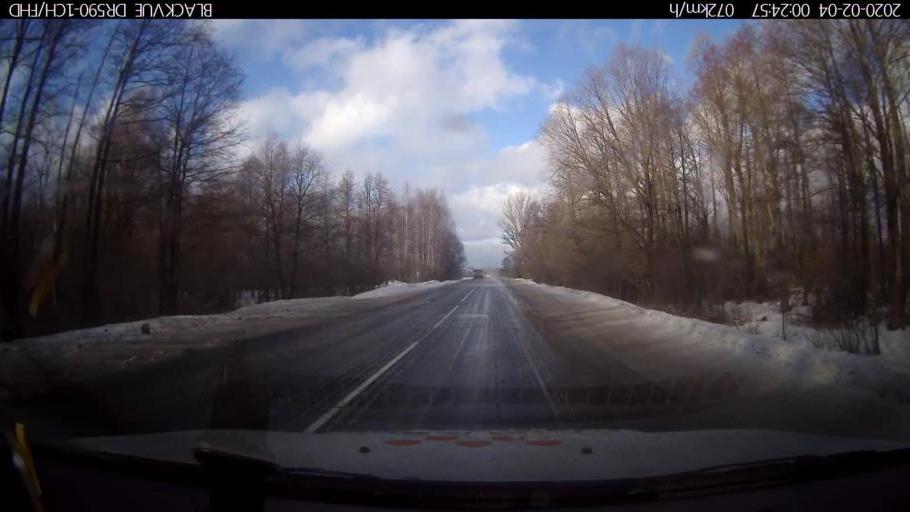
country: RU
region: Nizjnij Novgorod
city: Kstovo
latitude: 56.0007
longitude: 44.2112
